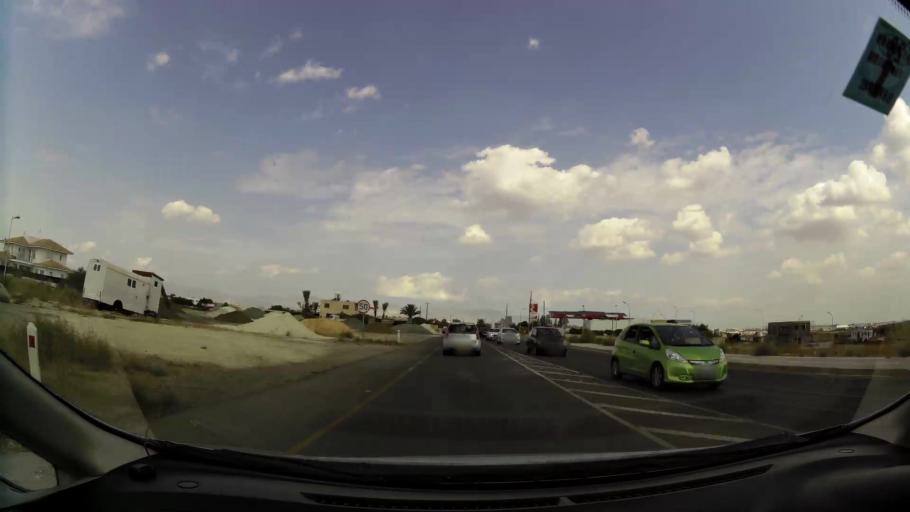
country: CY
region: Lefkosia
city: Tseri
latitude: 35.1054
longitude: 33.3298
